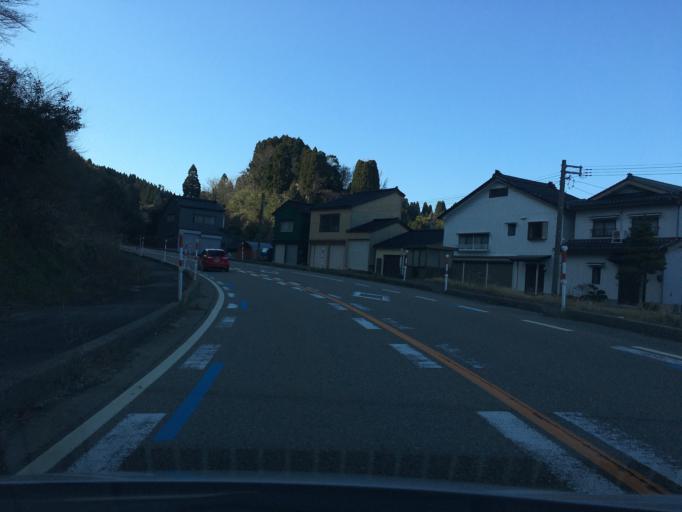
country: JP
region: Toyama
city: Himi
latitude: 36.9204
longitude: 137.0271
